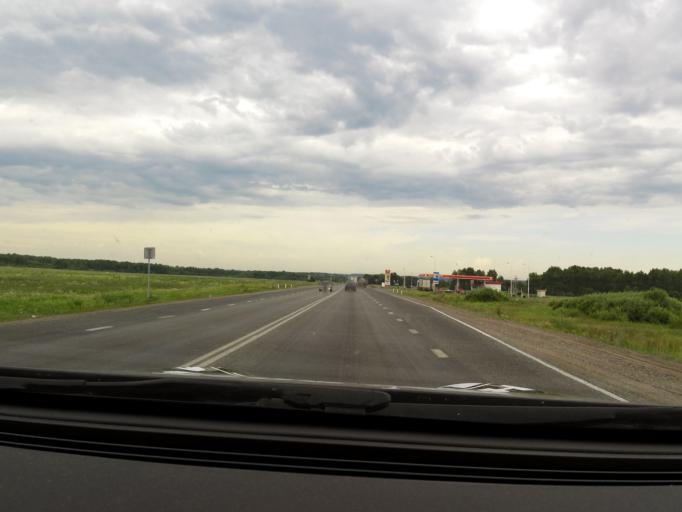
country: RU
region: Bashkortostan
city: Kudeyevskiy
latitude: 54.8173
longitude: 56.8080
